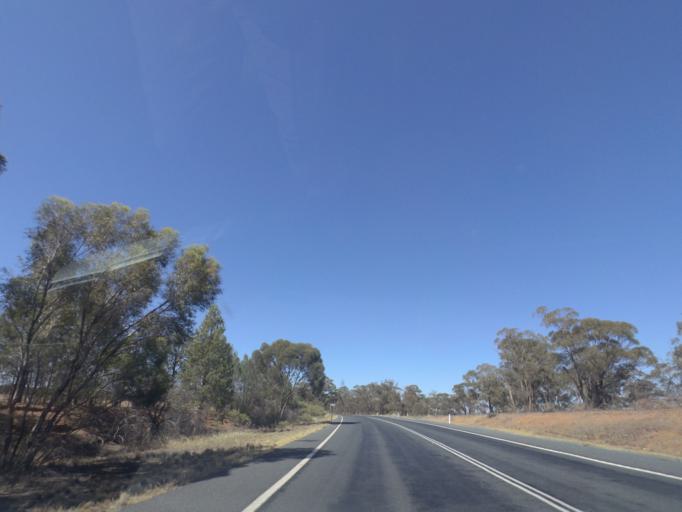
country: AU
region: New South Wales
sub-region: Bland
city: West Wyalong
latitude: -34.1178
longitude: 147.1299
